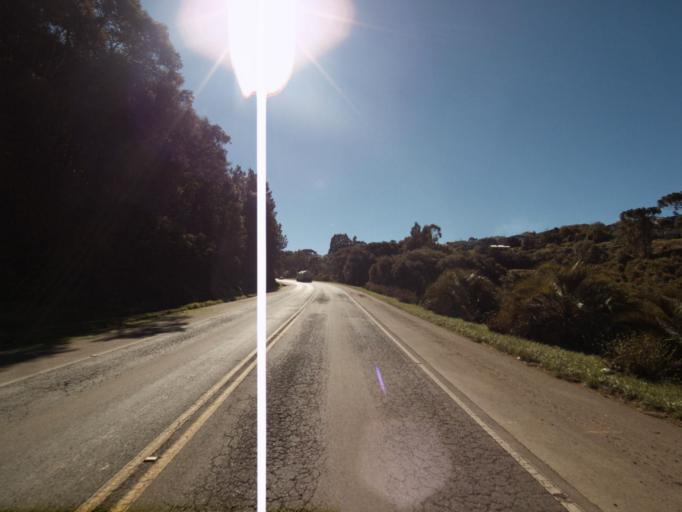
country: BR
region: Santa Catarina
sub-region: Joacaba
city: Joacaba
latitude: -27.0788
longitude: -51.6634
